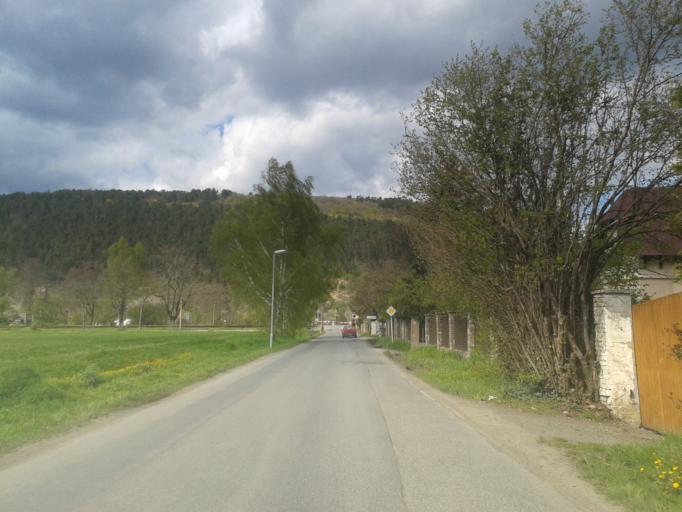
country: CZ
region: Central Bohemia
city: Revnice
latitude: 49.9308
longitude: 14.1796
